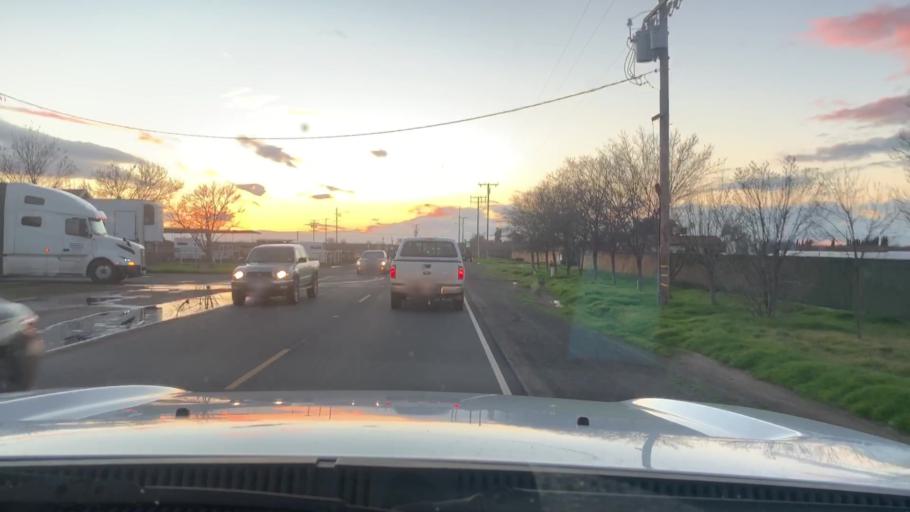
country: US
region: California
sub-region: Tulare County
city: Tulare
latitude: 36.2035
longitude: -119.4181
